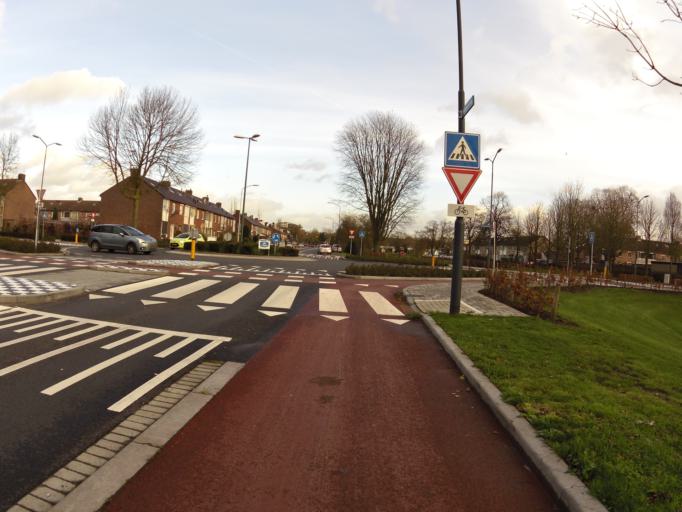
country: NL
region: North Brabant
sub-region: Gemeente Vught
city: Vught
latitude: 51.6430
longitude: 5.2862
